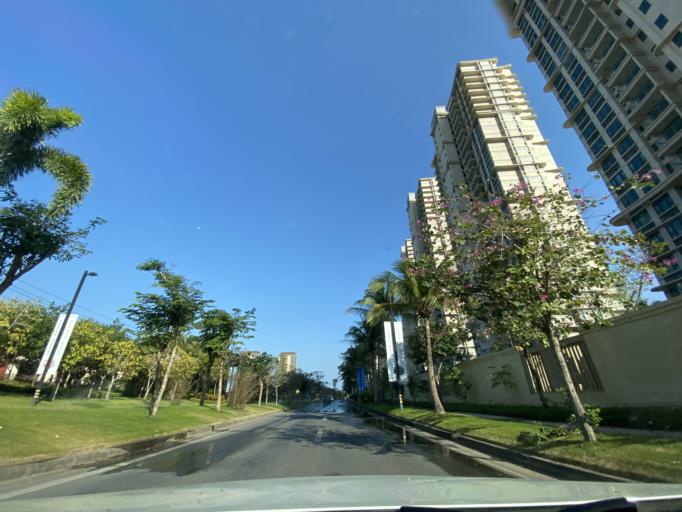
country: CN
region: Hainan
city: Xincun
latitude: 18.4239
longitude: 109.9346
